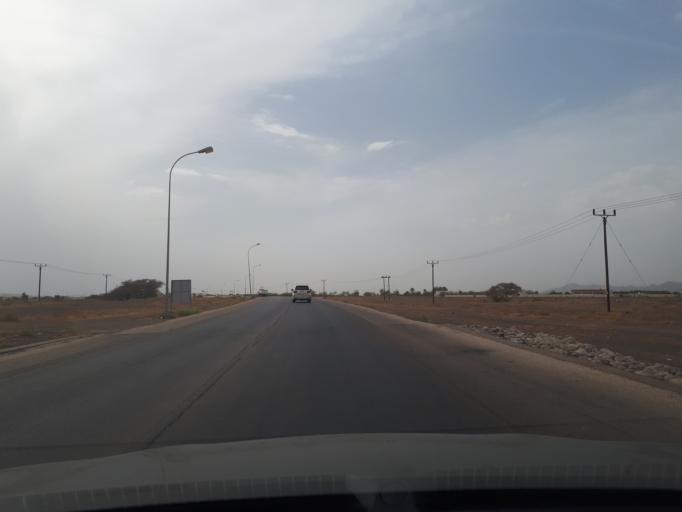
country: OM
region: Ash Sharqiyah
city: Badiyah
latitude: 22.4855
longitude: 58.7755
